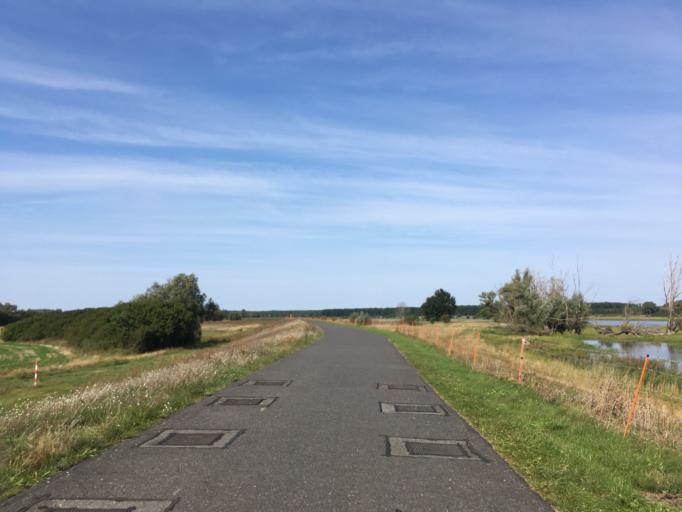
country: DE
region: Brandenburg
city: Neuzelle
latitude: 52.0748
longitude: 14.7464
